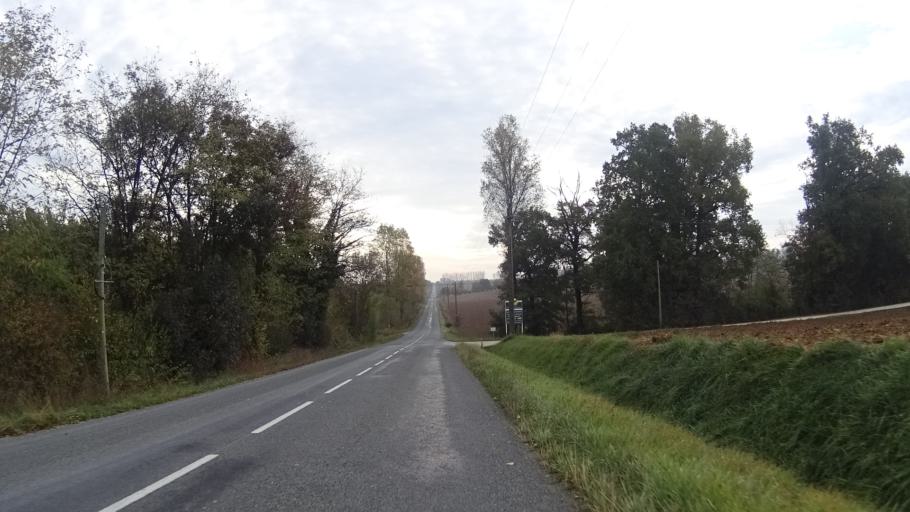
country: FR
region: Aquitaine
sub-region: Departement du Lot-et-Garonne
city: Laplume
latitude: 44.0943
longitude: 0.5722
